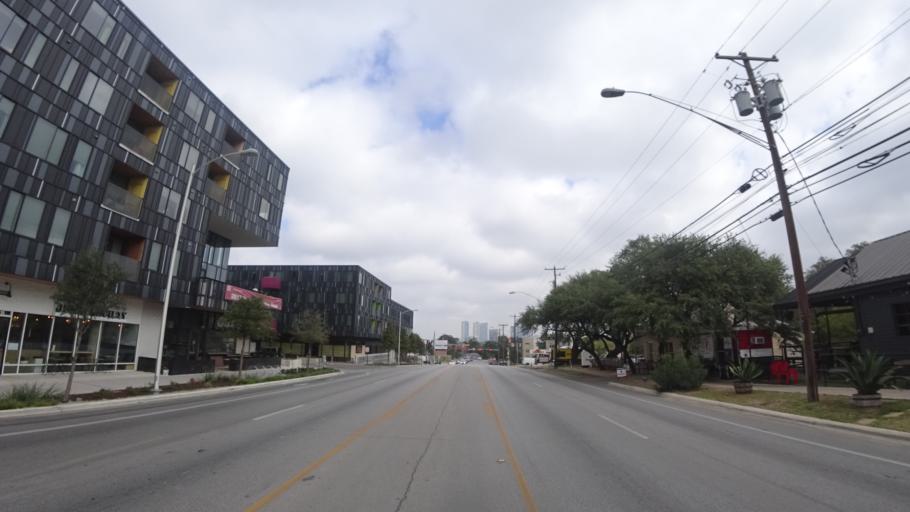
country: US
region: Texas
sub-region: Travis County
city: Austin
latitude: 30.2551
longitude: -97.7621
